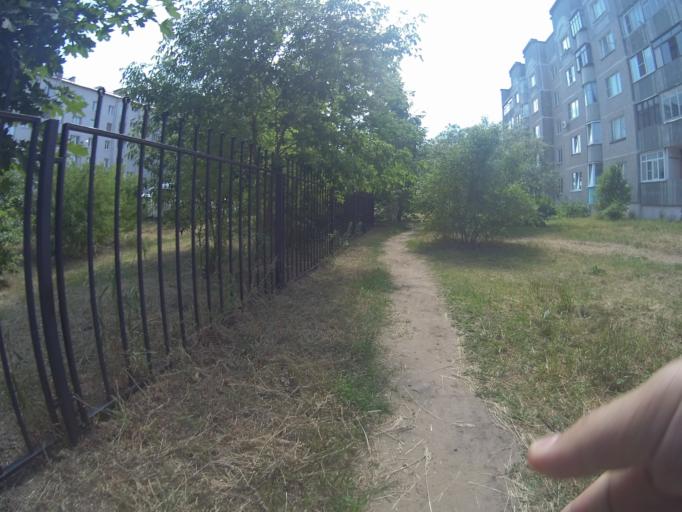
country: RU
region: Vladimir
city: Kommunar
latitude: 56.1076
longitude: 40.4474
